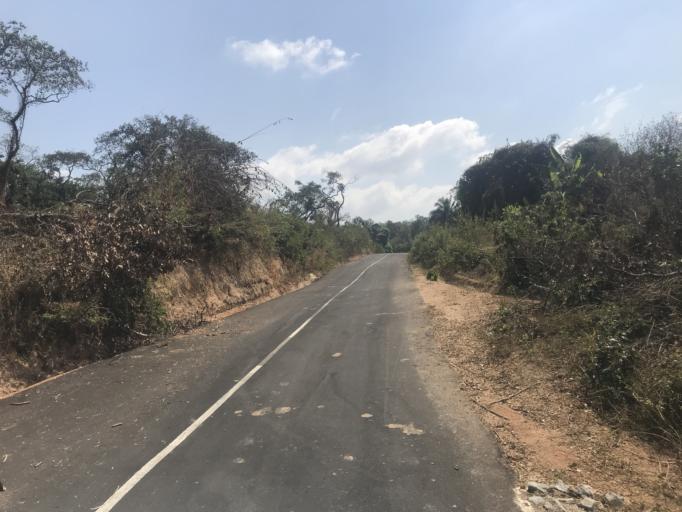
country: NG
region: Osun
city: Otan Ayegbaju
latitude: 7.8994
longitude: 4.8323
